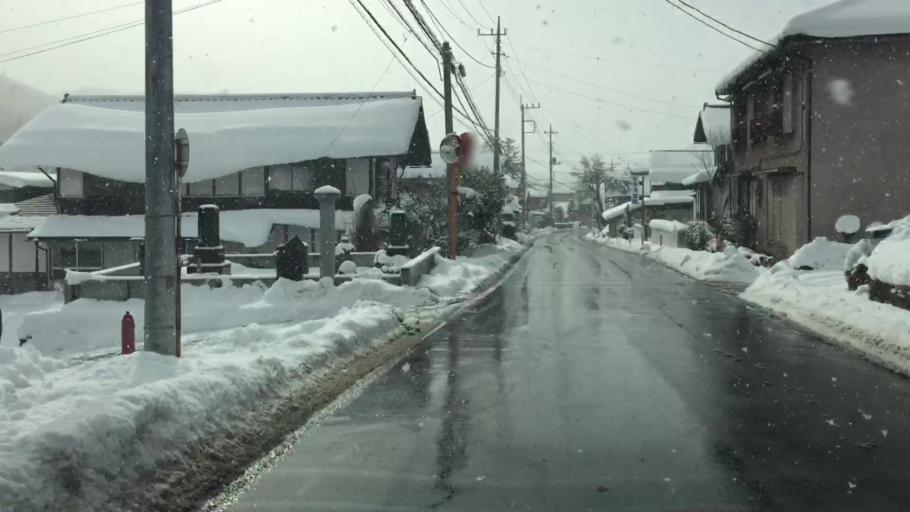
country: JP
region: Gunma
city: Numata
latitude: 36.6978
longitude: 139.0648
